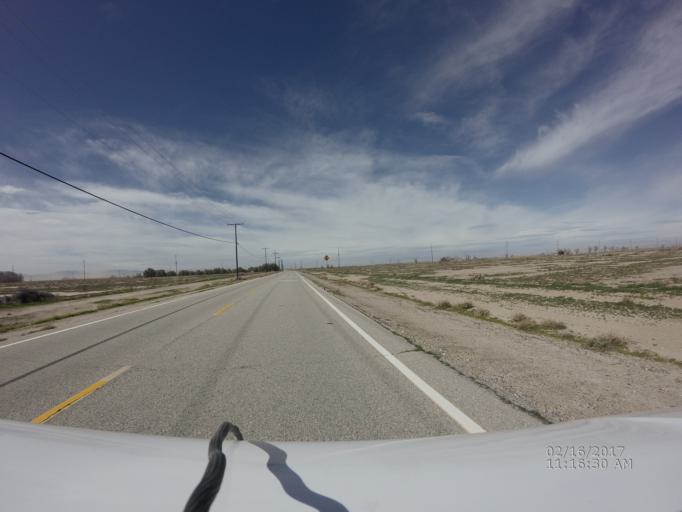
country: US
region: California
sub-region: Los Angeles County
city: Lancaster
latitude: 34.7198
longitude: -117.9669
